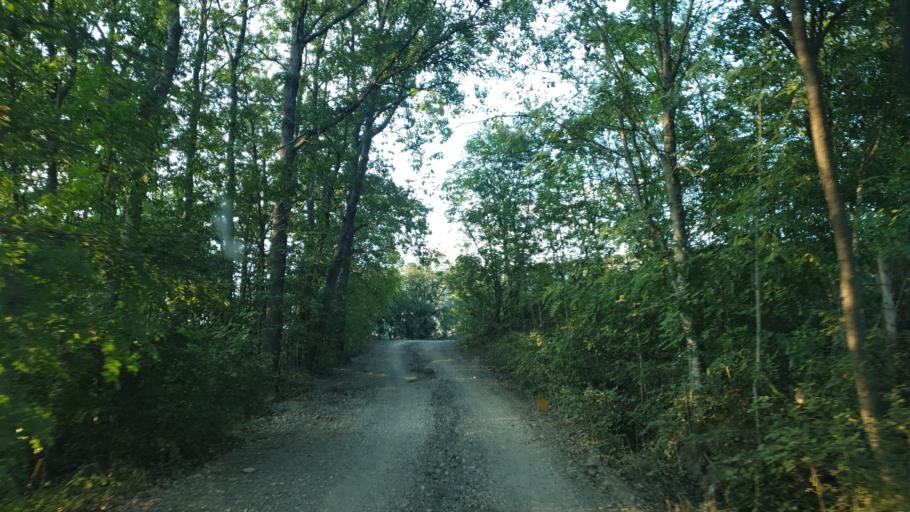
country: RS
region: Central Serbia
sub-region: Zlatiborski Okrug
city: Kosjeric
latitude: 43.9952
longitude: 20.0017
